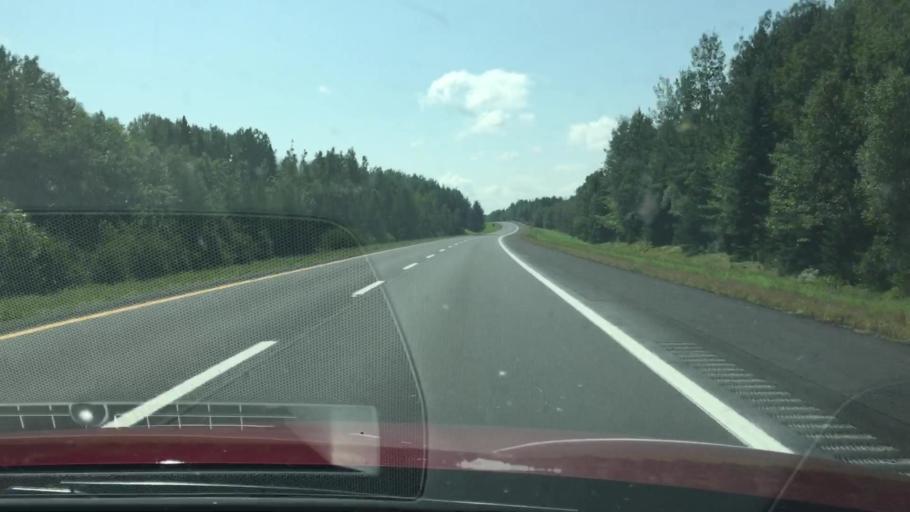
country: US
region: Maine
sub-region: Penobscot County
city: Patten
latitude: 45.9175
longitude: -68.3725
